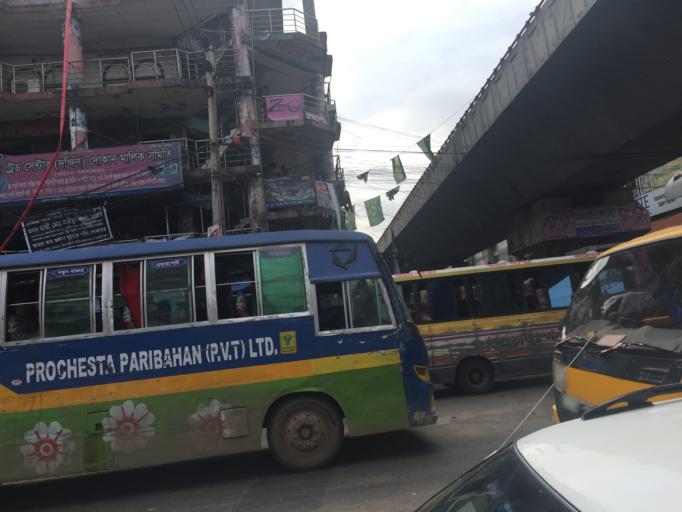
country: BD
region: Dhaka
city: Paltan
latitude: 23.7237
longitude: 90.4108
